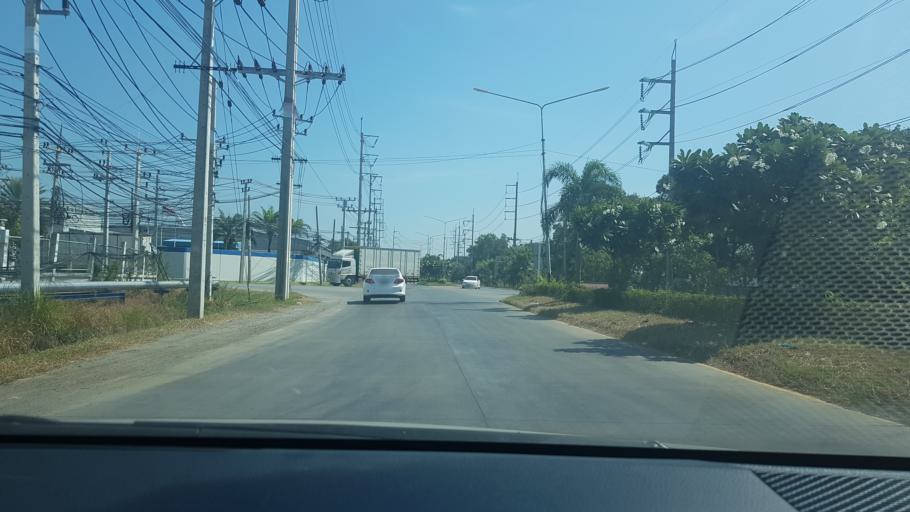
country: TH
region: Phra Nakhon Si Ayutthaya
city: Bang Pa-in
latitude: 14.2519
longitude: 100.6040
